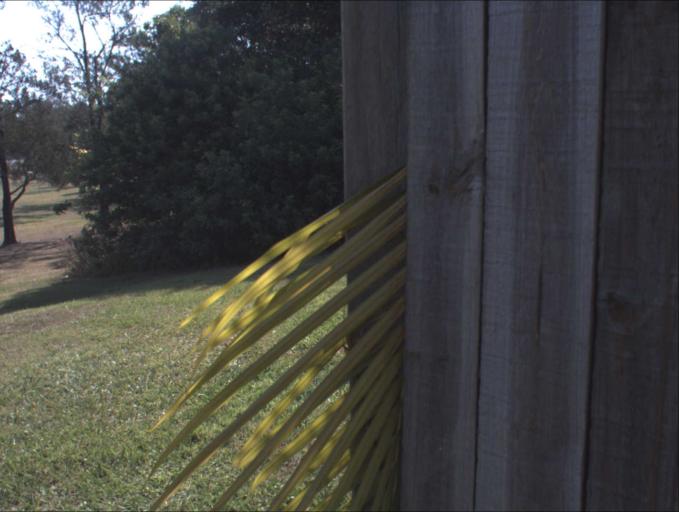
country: AU
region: Queensland
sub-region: Logan
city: Beenleigh
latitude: -27.6894
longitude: 153.1822
